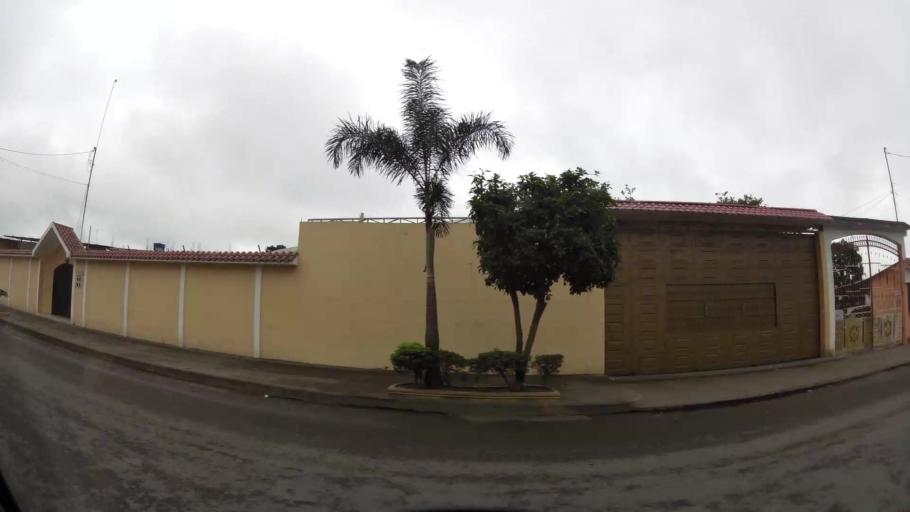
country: EC
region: El Oro
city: Pasaje
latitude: -3.3268
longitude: -79.8151
